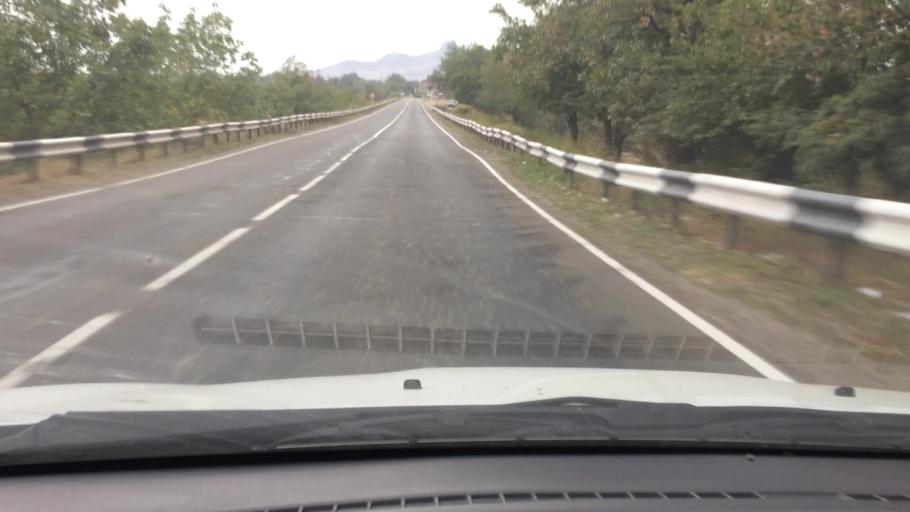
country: GE
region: Kvemo Kartli
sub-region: Marneuli
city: Marneuli
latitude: 41.4083
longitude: 44.8312
